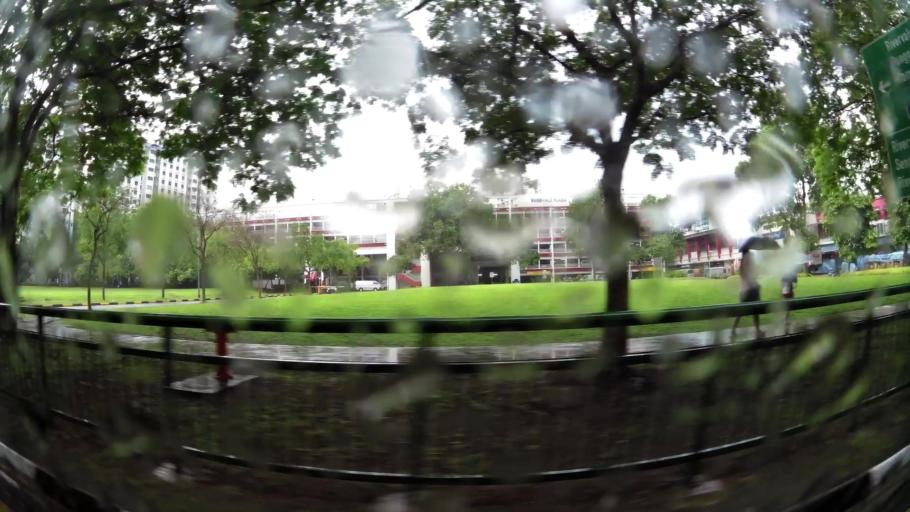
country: MY
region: Johor
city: Kampung Pasir Gudang Baru
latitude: 1.3849
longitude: 103.9026
